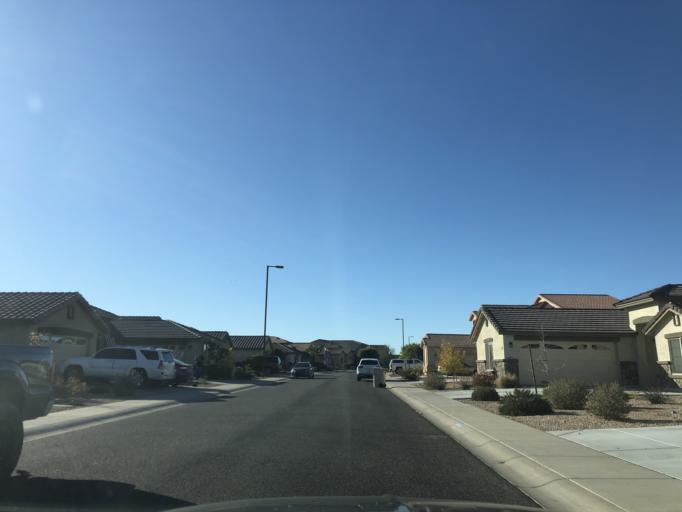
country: US
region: Arizona
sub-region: Maricopa County
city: Buckeye
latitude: 33.4244
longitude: -112.6046
